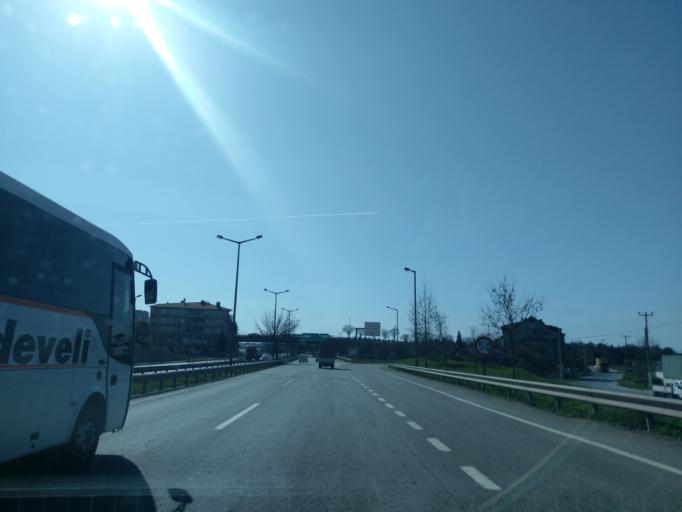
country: TR
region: Kocaeli
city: Darica
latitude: 40.8197
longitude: 29.3648
